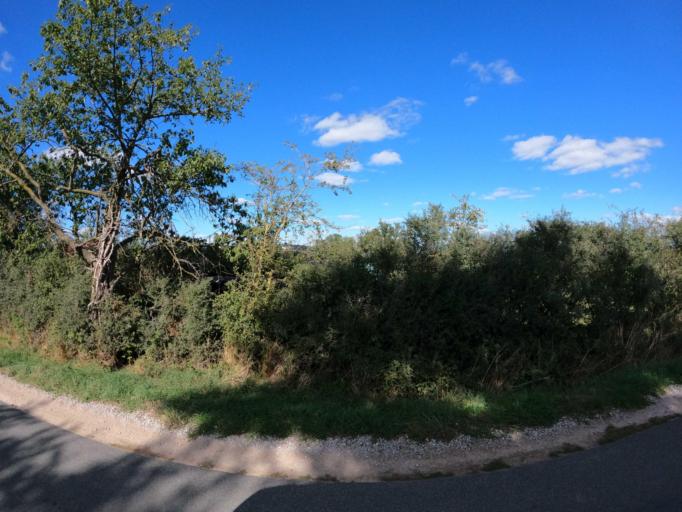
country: FR
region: Auvergne
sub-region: Departement de l'Allier
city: Doyet
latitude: 46.3999
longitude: 2.7478
